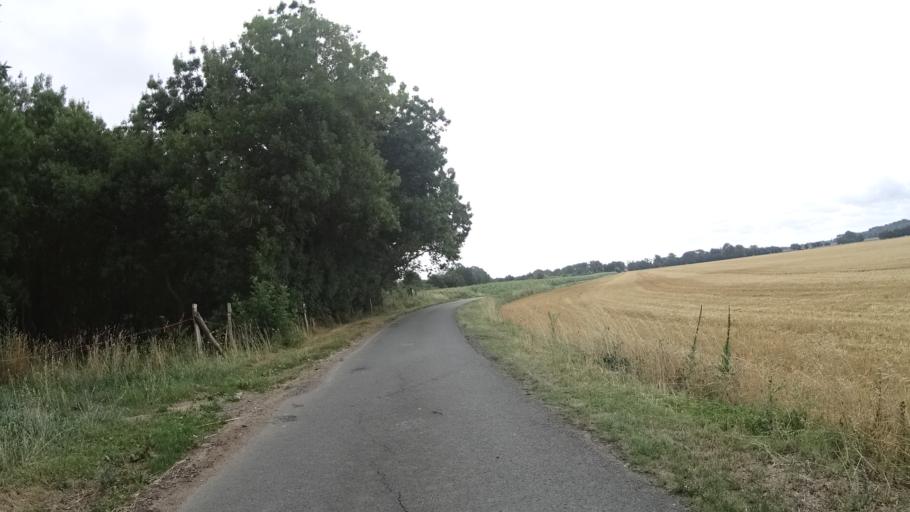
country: FR
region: Pays de la Loire
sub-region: Departement de Maine-et-Loire
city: Saint-Germain-des-Pres
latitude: 47.3779
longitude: -0.8016
